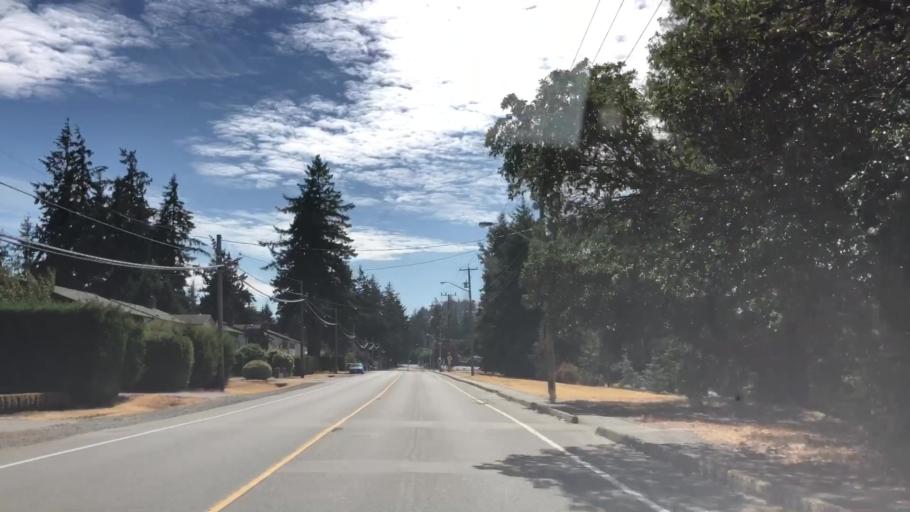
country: CA
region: British Columbia
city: Colwood
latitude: 48.4240
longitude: -123.4919
